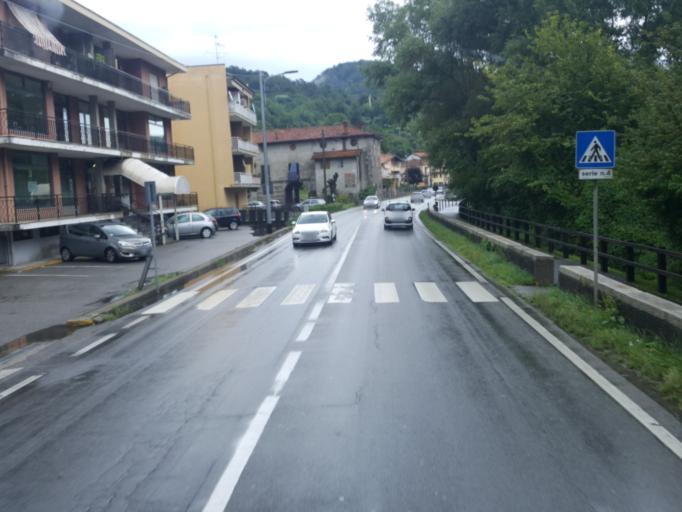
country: IT
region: Piedmont
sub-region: Provincia Verbano-Cusio-Ossola
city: Cossogno
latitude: 45.9456
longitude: 8.4924
